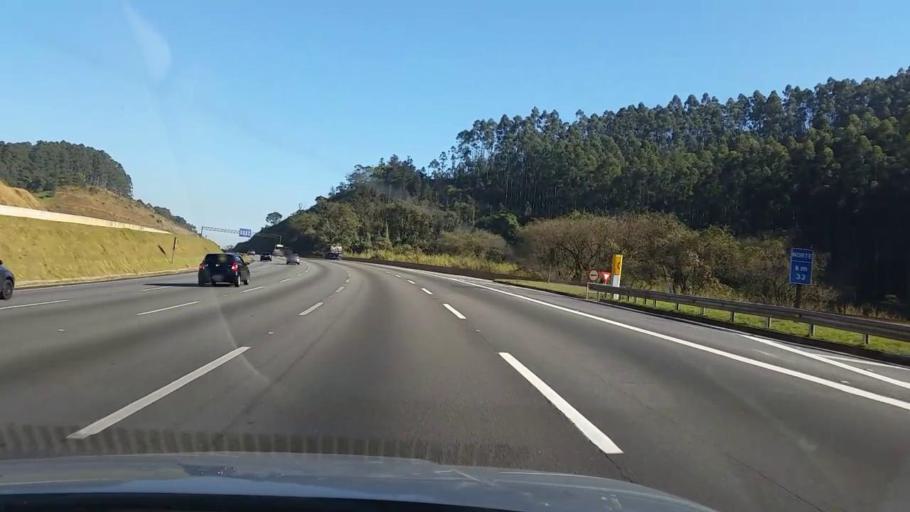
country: BR
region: Sao Paulo
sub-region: Caieiras
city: Caieiras
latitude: -23.3575
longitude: -46.7865
